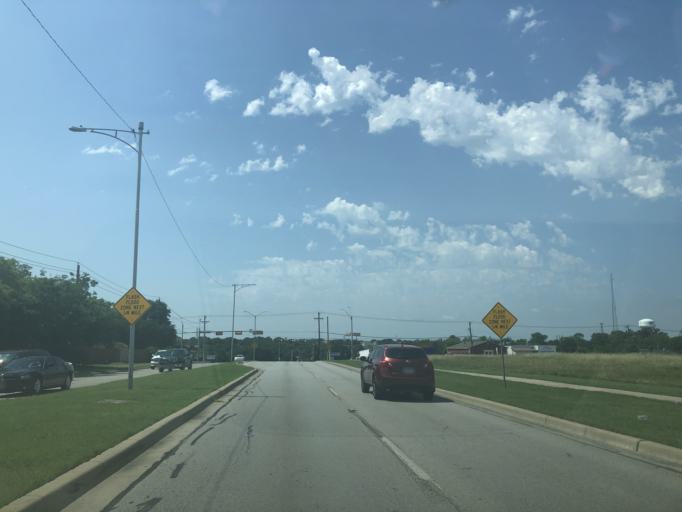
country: US
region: Texas
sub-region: Dallas County
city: Grand Prairie
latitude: 32.7300
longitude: -97.0147
